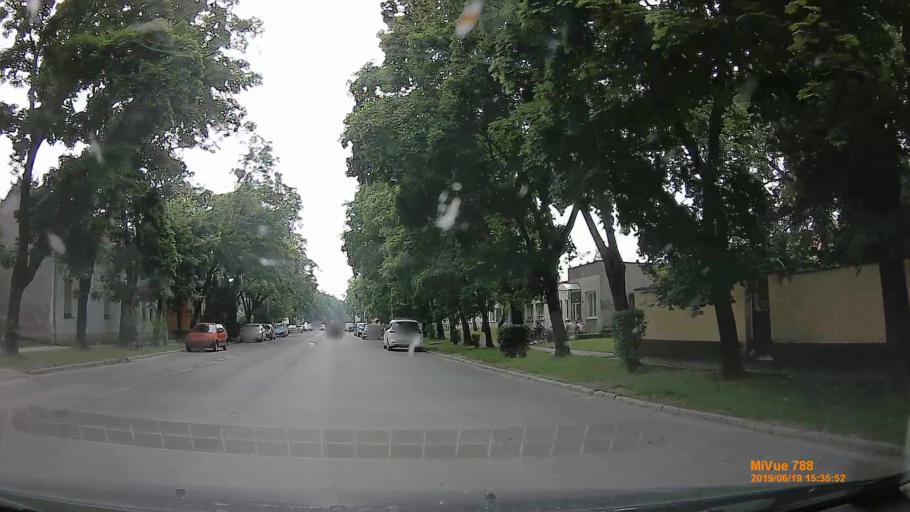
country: HU
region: Baranya
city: Szigetvar
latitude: 46.0479
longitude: 17.8089
